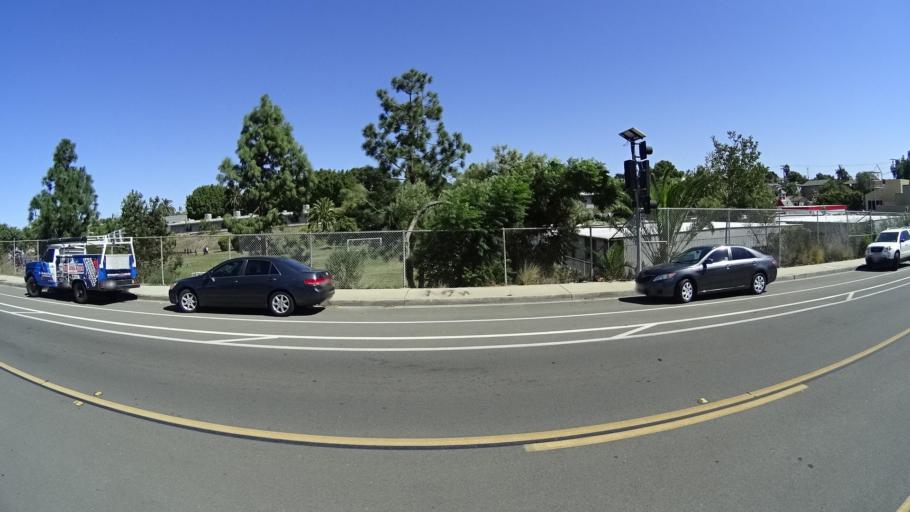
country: US
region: California
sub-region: San Diego County
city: National City
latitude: 32.6701
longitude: -117.0774
